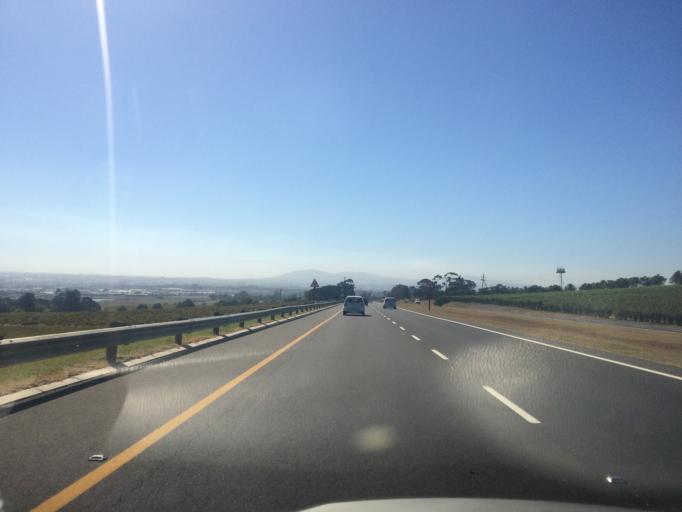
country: ZA
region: Western Cape
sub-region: City of Cape Town
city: Kraaifontein
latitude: -33.9603
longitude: 18.7263
